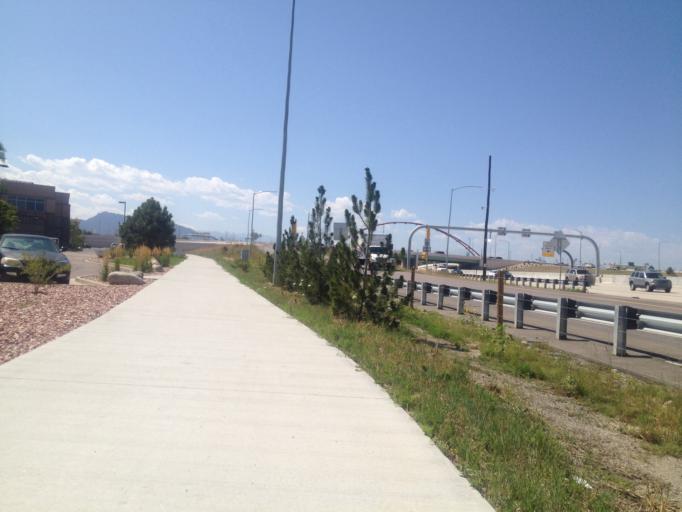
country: US
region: Colorado
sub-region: Boulder County
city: Superior
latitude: 39.9564
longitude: -105.1631
